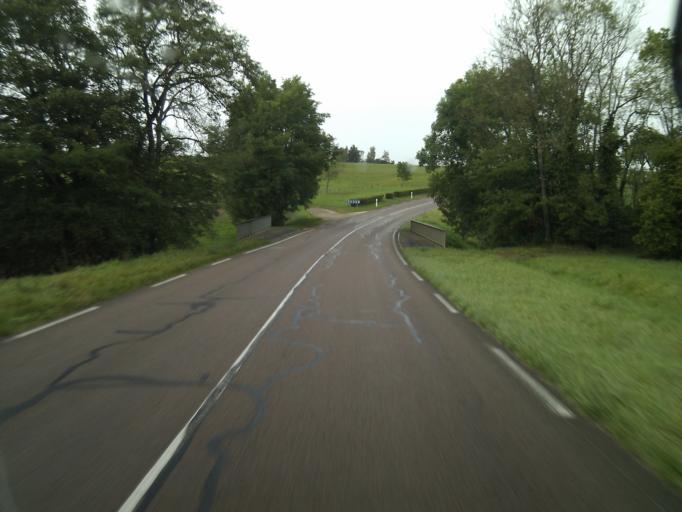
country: FR
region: Bourgogne
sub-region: Departement de la Cote-d'Or
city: Semur-en-Auxois
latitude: 47.4872
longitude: 4.3189
